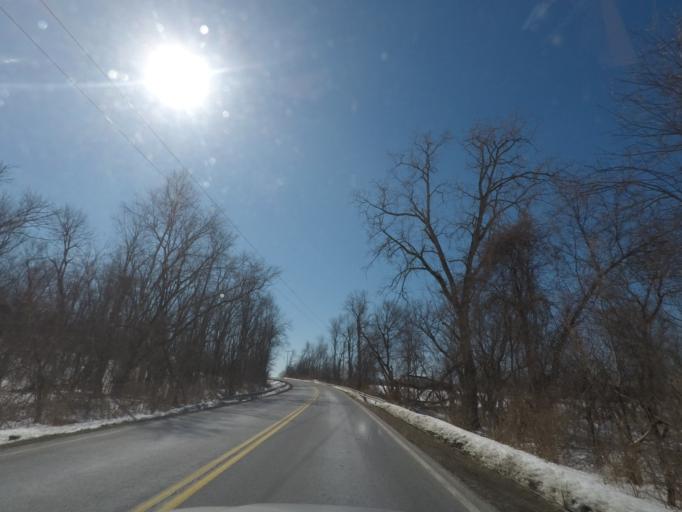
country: US
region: New York
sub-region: Saratoga County
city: Stillwater
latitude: 42.9642
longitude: -73.6221
